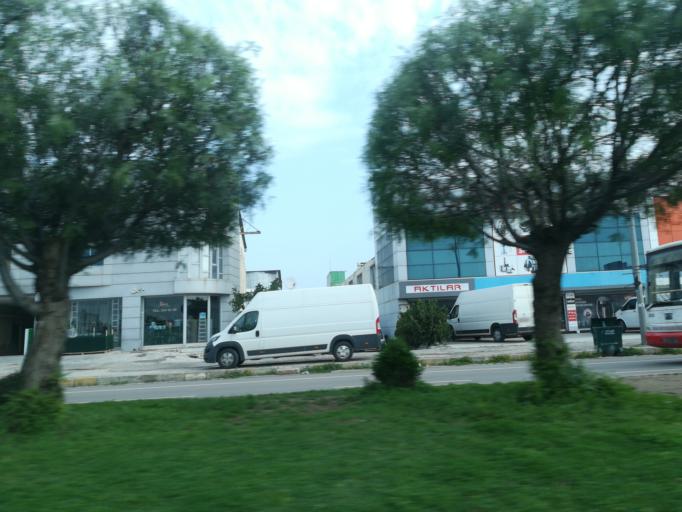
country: TR
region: Adana
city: Yuregir
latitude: 36.9855
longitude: 35.3654
